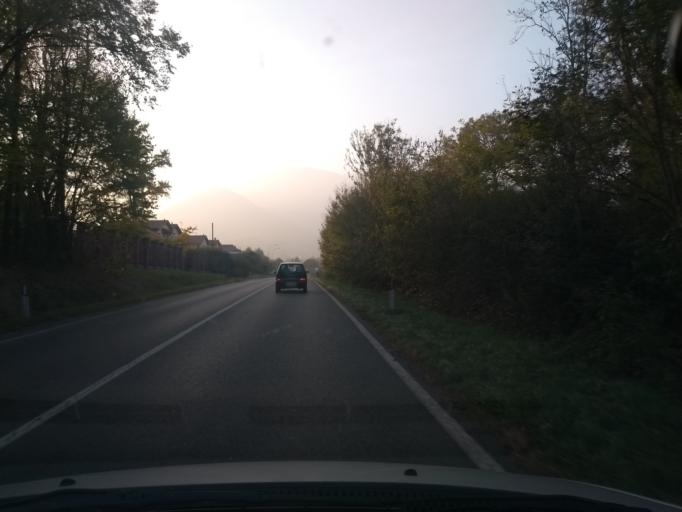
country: IT
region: Piedmont
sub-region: Provincia di Torino
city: Givoletto
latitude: 45.1517
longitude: 7.5121
